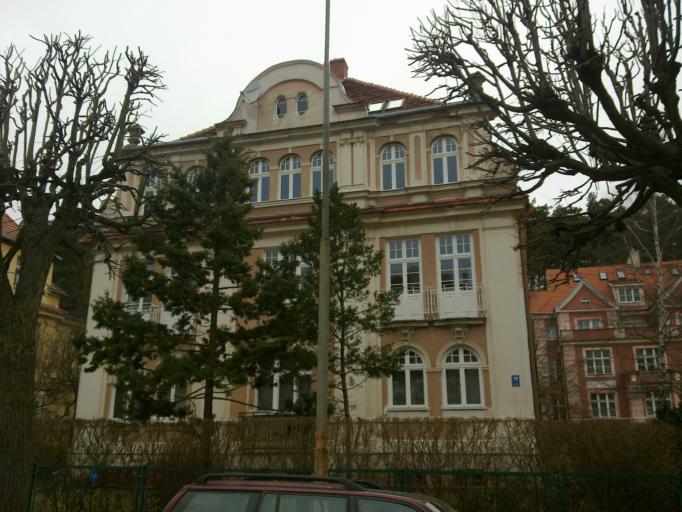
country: PL
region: Pomeranian Voivodeship
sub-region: Sopot
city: Sopot
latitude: 54.4371
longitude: 18.5552
